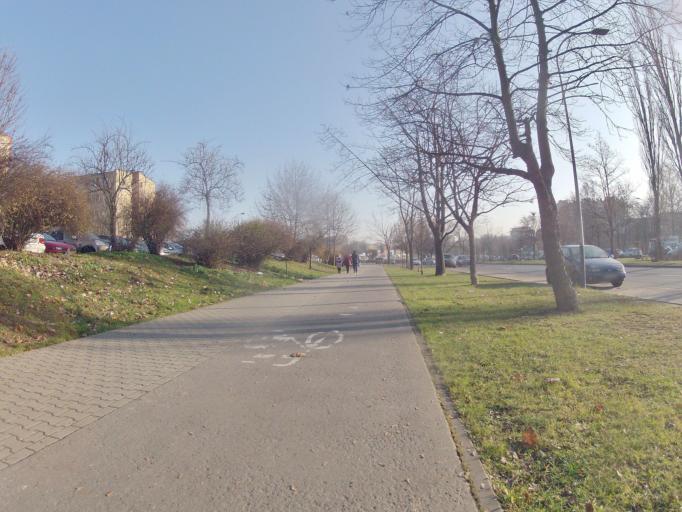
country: PL
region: Lesser Poland Voivodeship
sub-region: Powiat krakowski
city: Michalowice
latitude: 50.0860
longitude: 20.0159
